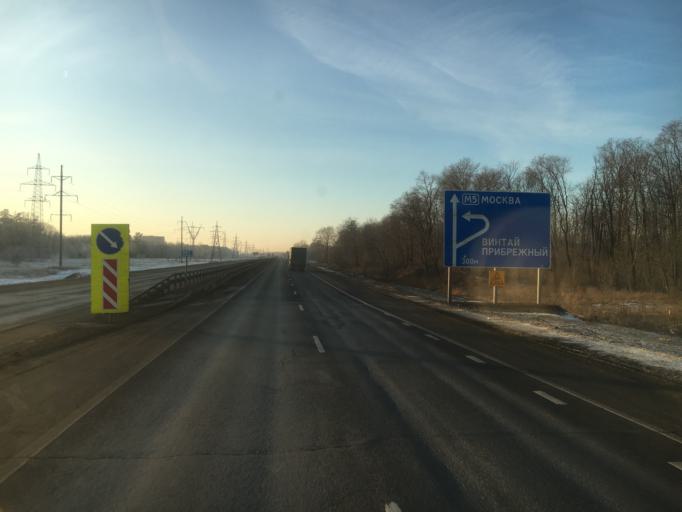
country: RU
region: Samara
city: Pribrezhnyy
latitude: 53.5169
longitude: 49.8489
